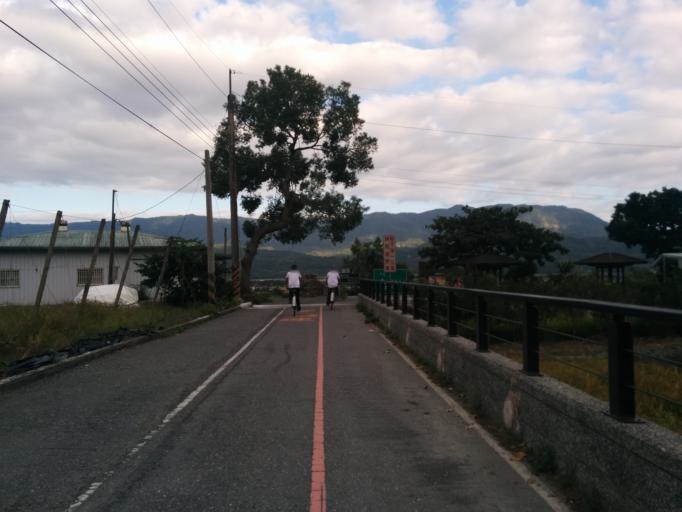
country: TW
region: Taiwan
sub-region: Taitung
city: Taitung
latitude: 23.0366
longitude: 121.1542
